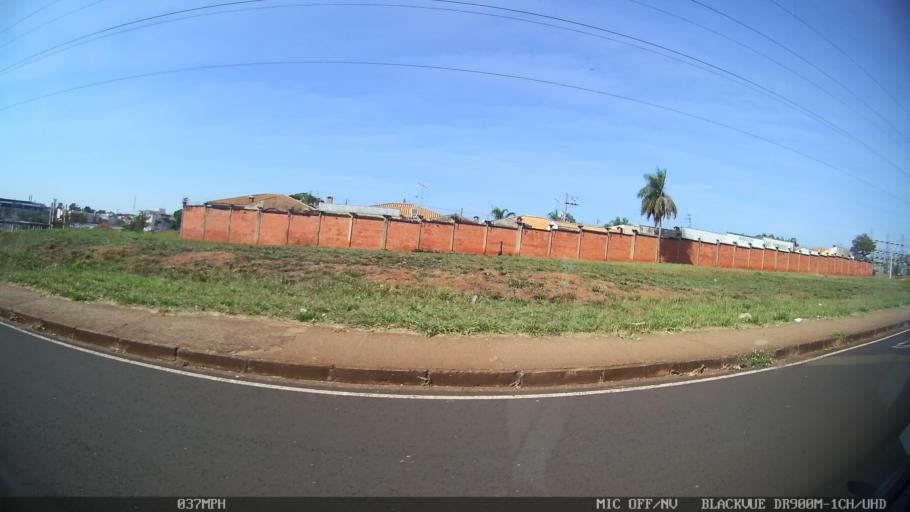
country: BR
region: Sao Paulo
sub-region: Sao Jose Do Rio Preto
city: Sao Jose do Rio Preto
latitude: -20.7870
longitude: -49.3819
